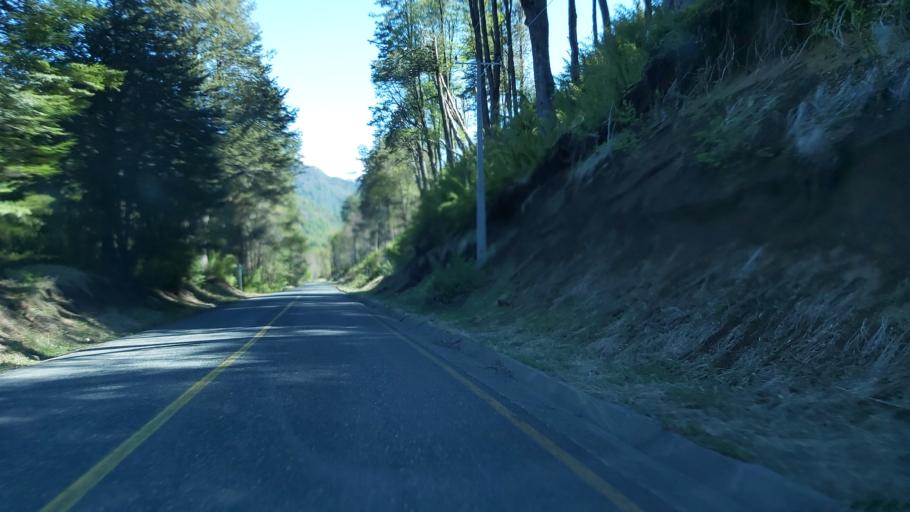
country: CL
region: Araucania
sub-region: Provincia de Cautin
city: Vilcun
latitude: -38.4618
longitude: -71.5168
